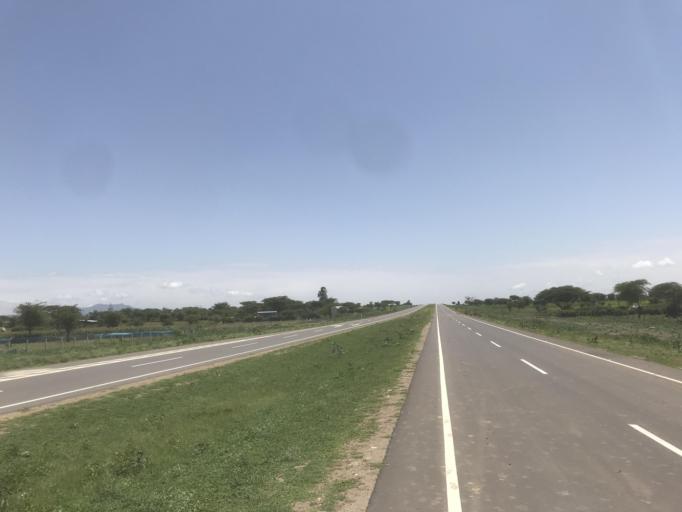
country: ET
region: Oromiya
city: Mojo
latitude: 8.3707
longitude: 38.9967
